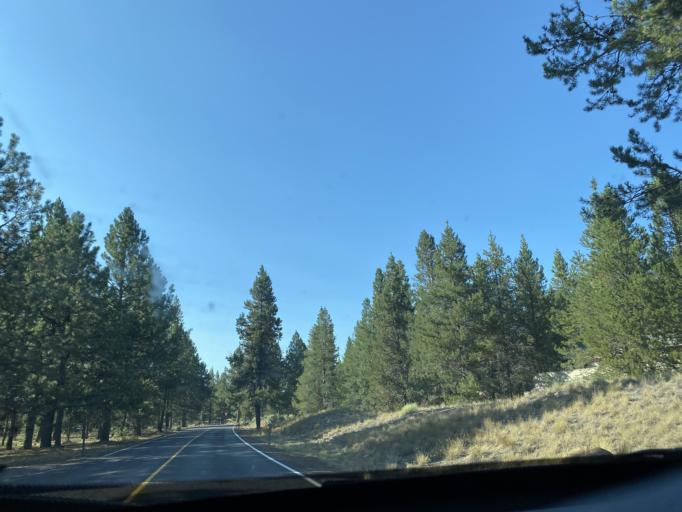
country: US
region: Oregon
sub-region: Deschutes County
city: Sunriver
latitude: 43.8810
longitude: -121.4380
